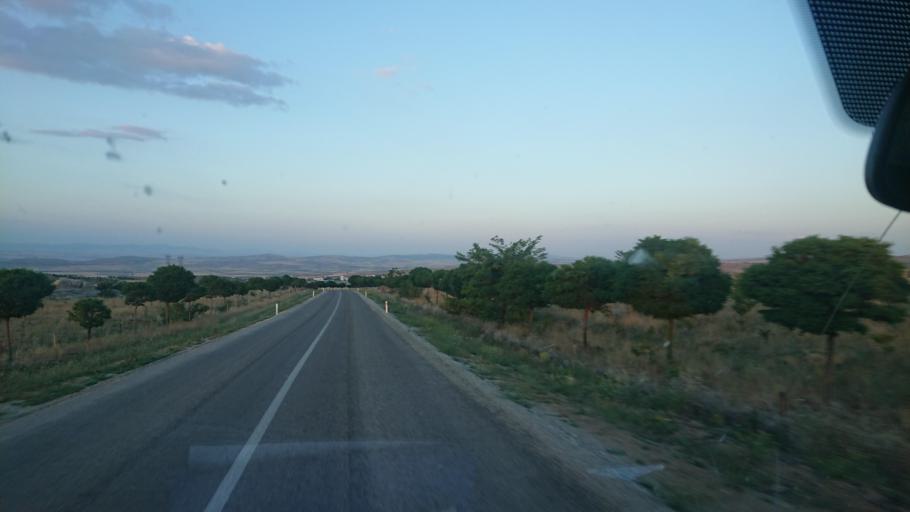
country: TR
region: Aksaray
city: Sariyahsi
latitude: 38.9697
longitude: 33.8069
